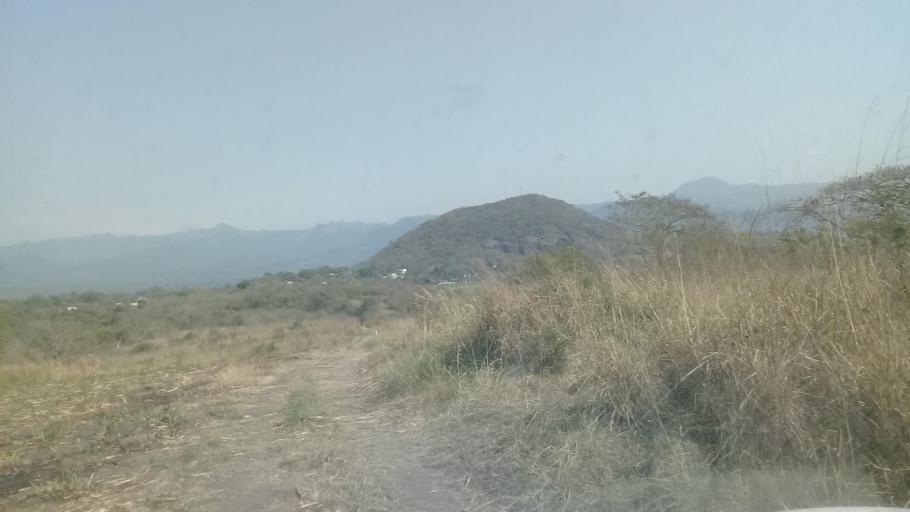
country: MX
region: Veracruz
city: El Castillo
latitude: 19.5758
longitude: -96.8327
